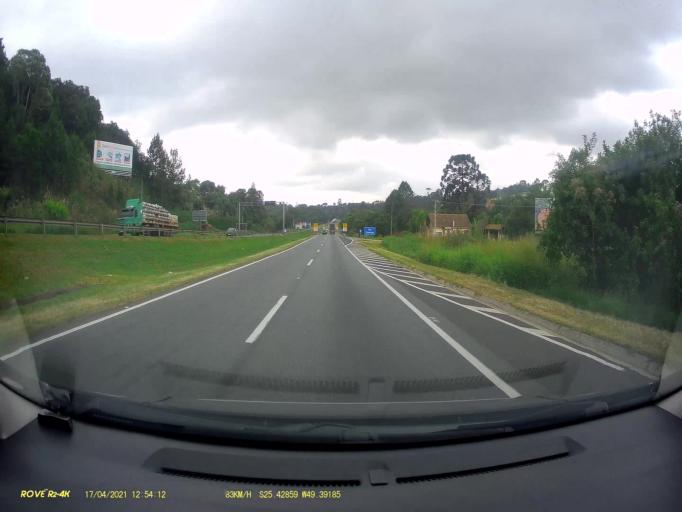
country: BR
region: Parana
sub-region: Curitiba
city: Curitiba
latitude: -25.4286
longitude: -49.3918
